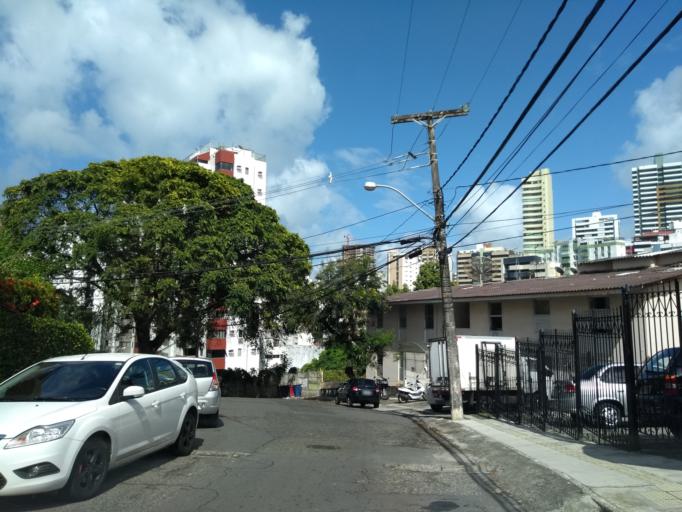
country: BR
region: Bahia
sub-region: Salvador
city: Salvador
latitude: -13.0017
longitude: -38.5190
